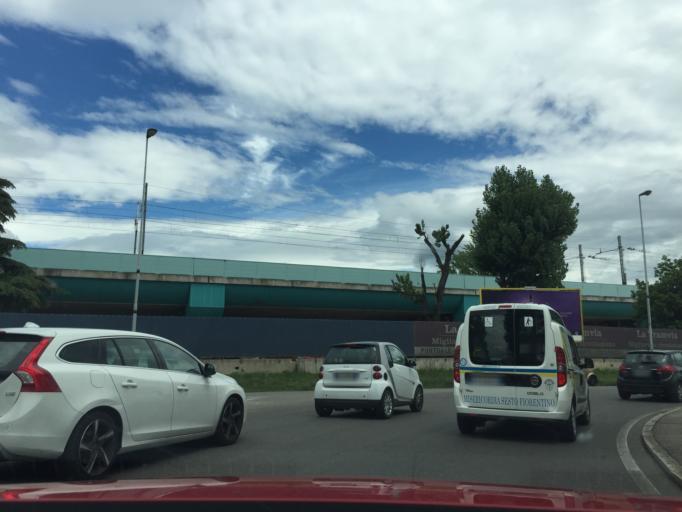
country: IT
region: Tuscany
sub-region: Province of Florence
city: Sesto Fiorentino
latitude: 43.8000
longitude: 11.2037
